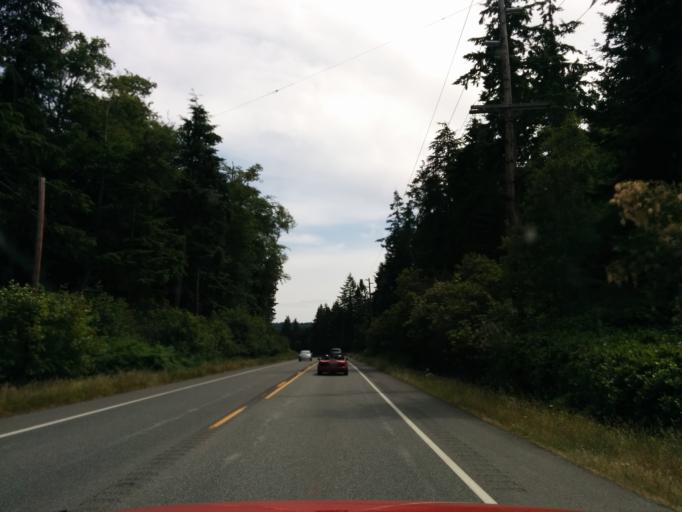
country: US
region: Washington
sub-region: Island County
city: Camano
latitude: 48.1204
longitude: -122.5875
